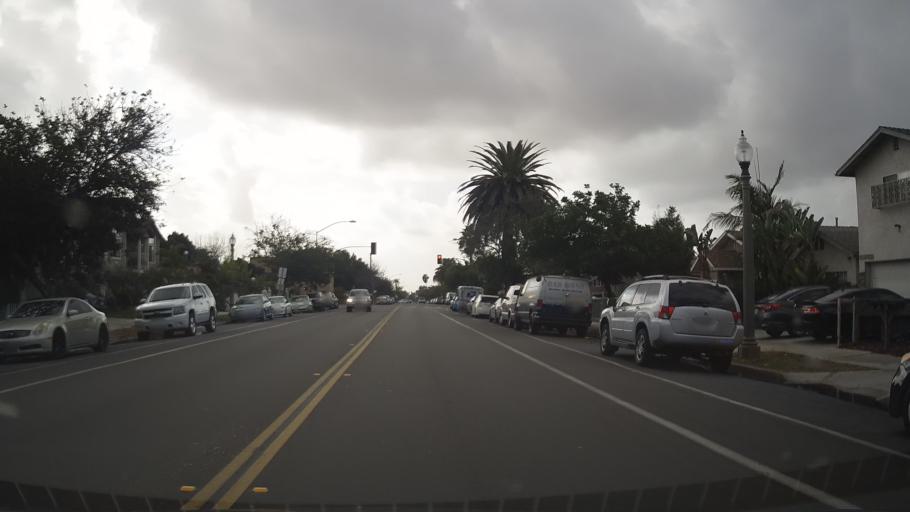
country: US
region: California
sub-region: San Diego County
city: San Diego
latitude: 32.7543
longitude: -117.1180
